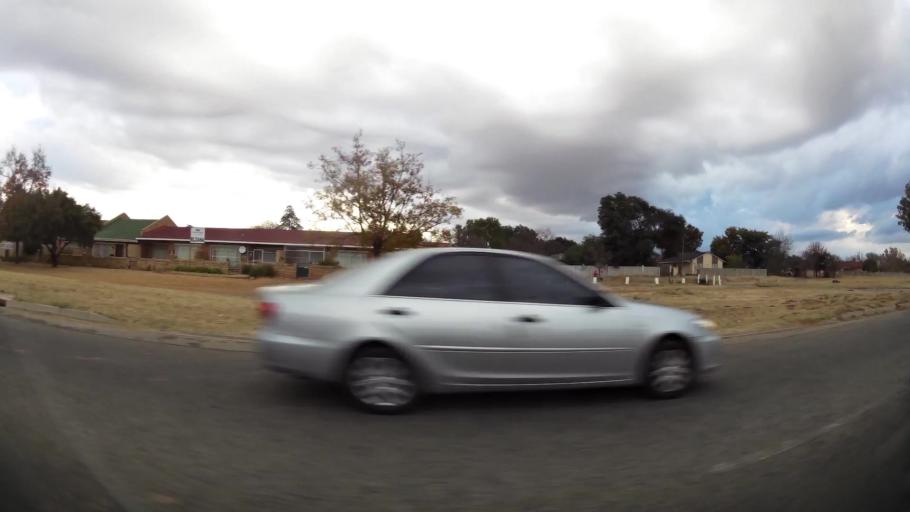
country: ZA
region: Orange Free State
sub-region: Lejweleputswa District Municipality
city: Welkom
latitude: -27.9644
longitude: 26.7261
